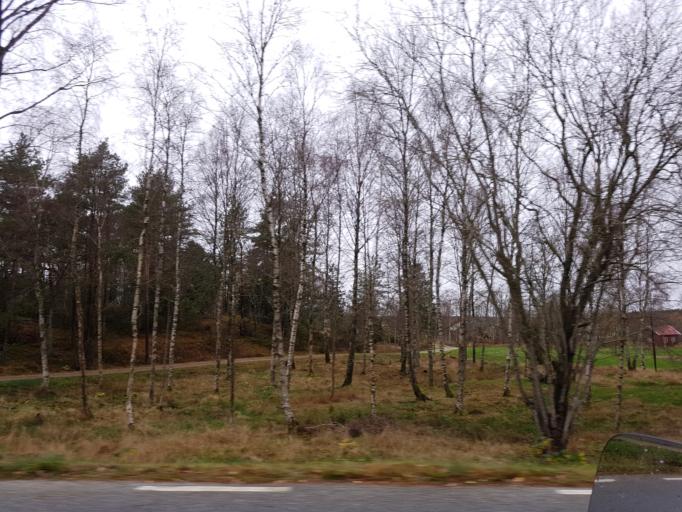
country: SE
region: Vaestra Goetaland
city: Svanesund
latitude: 58.1631
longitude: 11.7902
